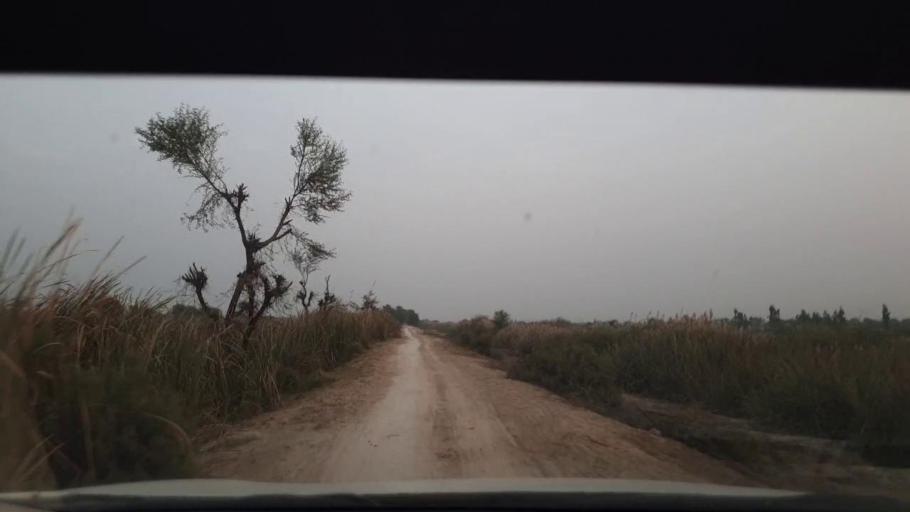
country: PK
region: Sindh
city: Berani
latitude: 25.8523
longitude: 68.7821
